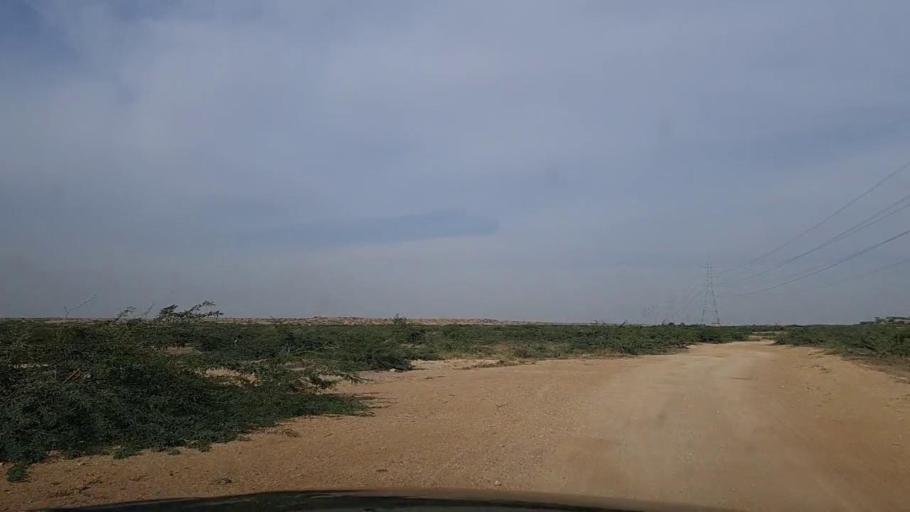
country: PK
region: Sindh
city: Gharo
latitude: 24.7794
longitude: 67.5576
